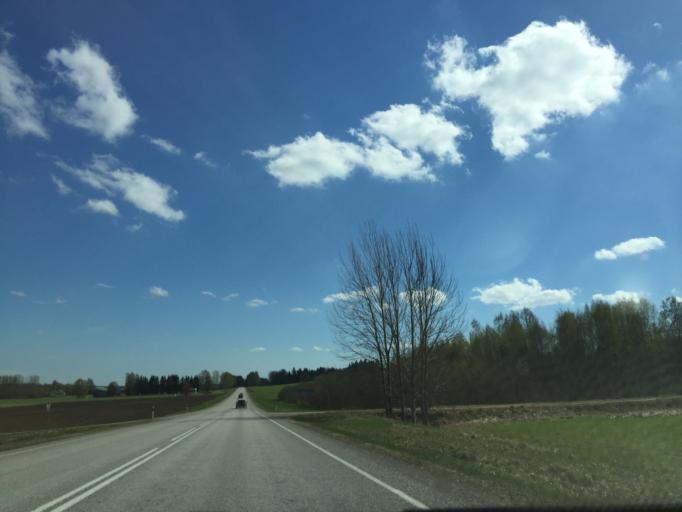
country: EE
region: Valgamaa
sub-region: Valga linn
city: Valga
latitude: 57.8984
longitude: 26.0513
